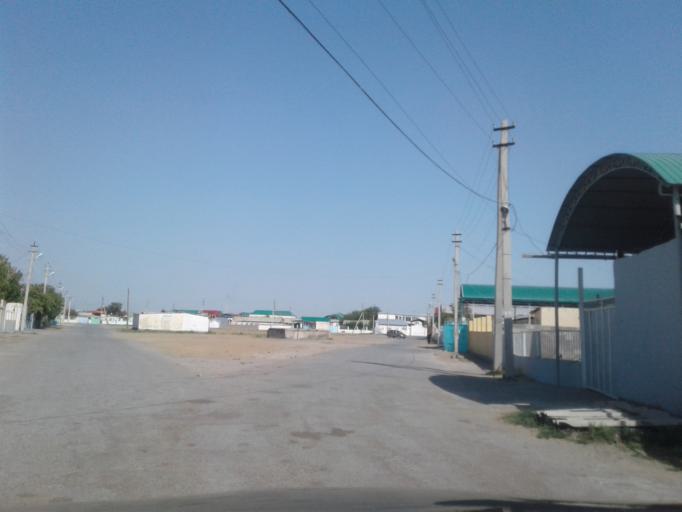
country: TM
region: Ahal
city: Ashgabat
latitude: 37.9740
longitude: 58.4354
